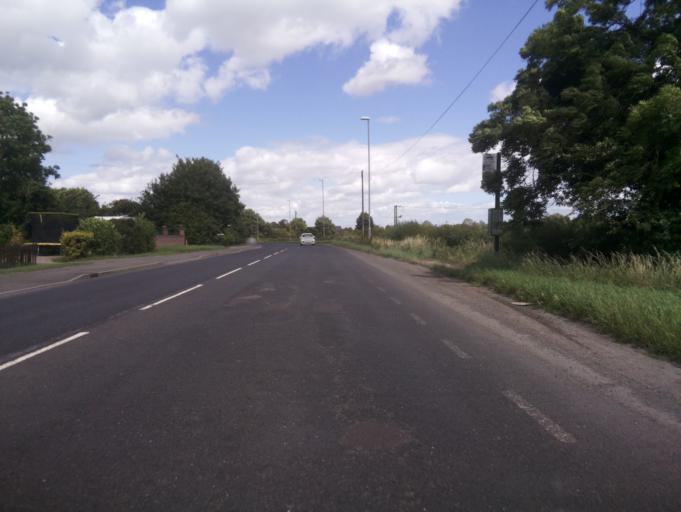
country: GB
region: England
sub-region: Nottinghamshire
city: Lowdham
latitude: 53.0045
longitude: -1.0077
